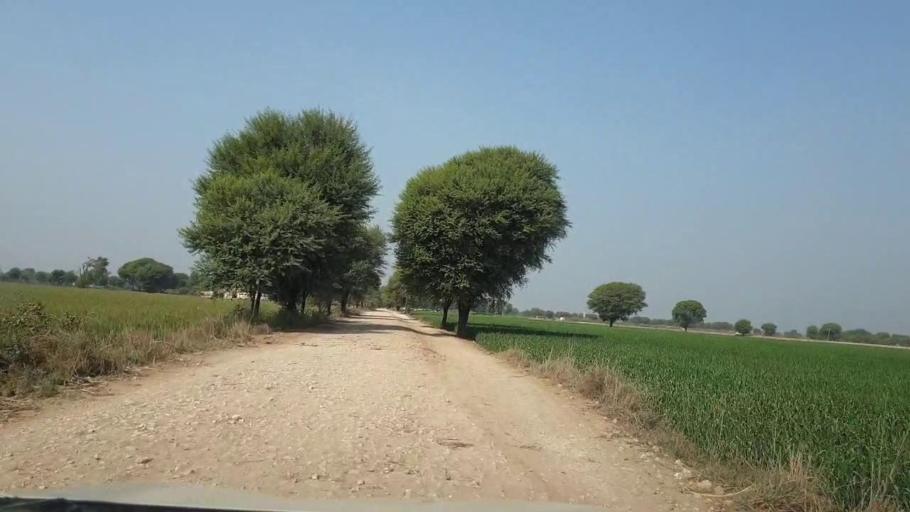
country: PK
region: Sindh
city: Bhit Shah
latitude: 25.7483
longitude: 68.4577
